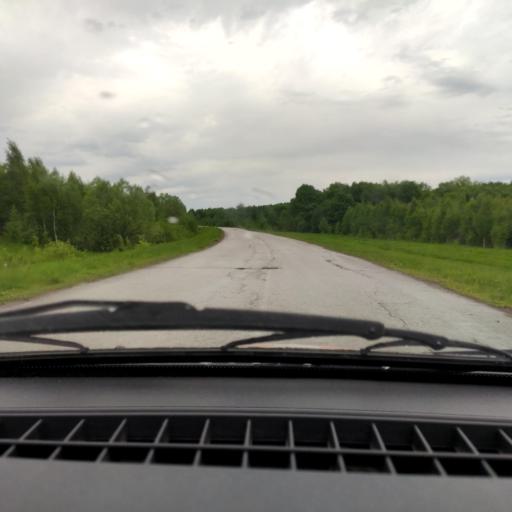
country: RU
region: Bashkortostan
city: Urman
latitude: 54.8570
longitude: 56.8313
